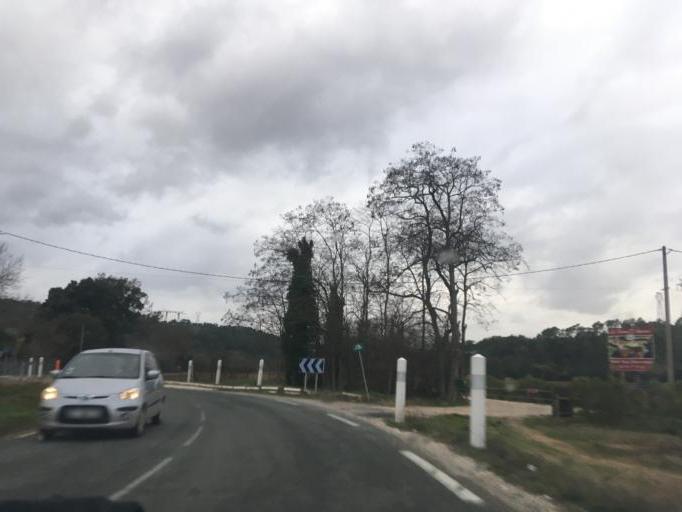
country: FR
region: Provence-Alpes-Cote d'Azur
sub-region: Departement du Var
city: Sainte-Anastasie-sur-Issole
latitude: 43.3397
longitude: 6.1459
